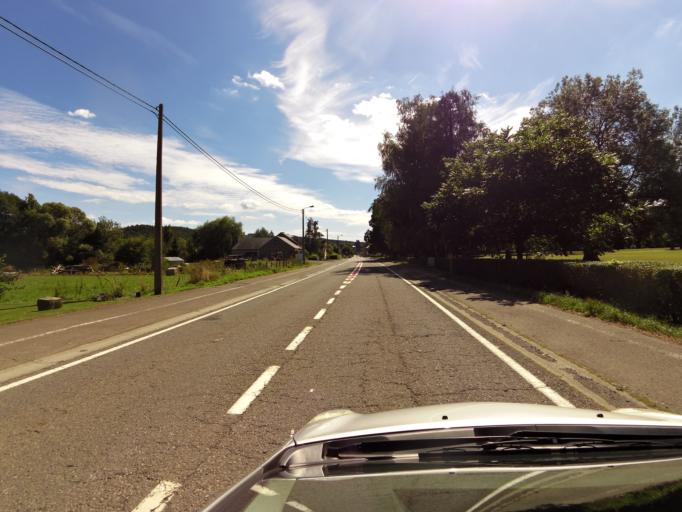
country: BE
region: Wallonia
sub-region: Province du Luxembourg
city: Rendeux
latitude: 50.2373
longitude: 5.5062
